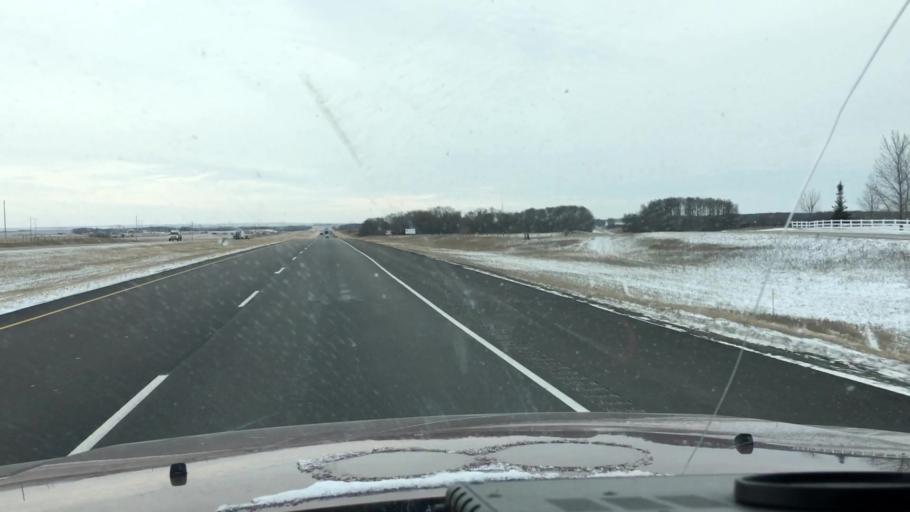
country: CA
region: Saskatchewan
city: Saskatoon
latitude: 51.9048
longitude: -106.5236
